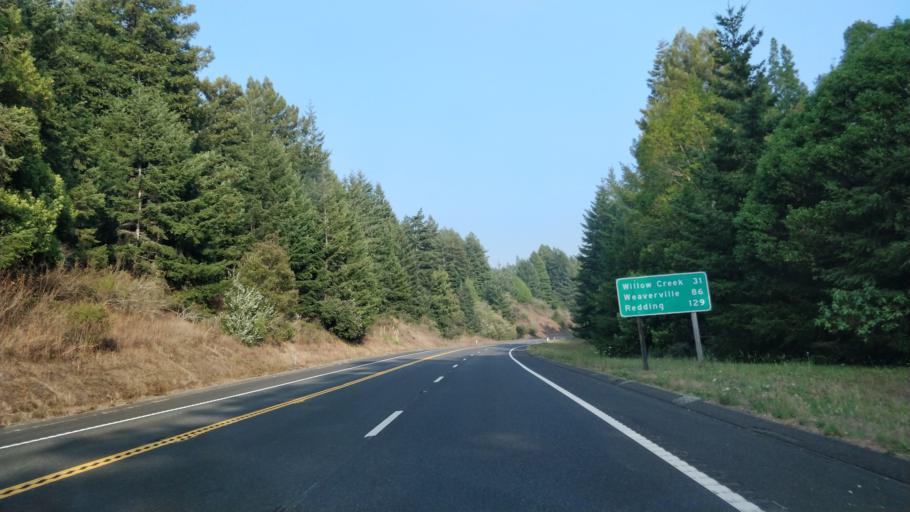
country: US
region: California
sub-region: Humboldt County
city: Blue Lake
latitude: 40.8880
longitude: -123.9800
